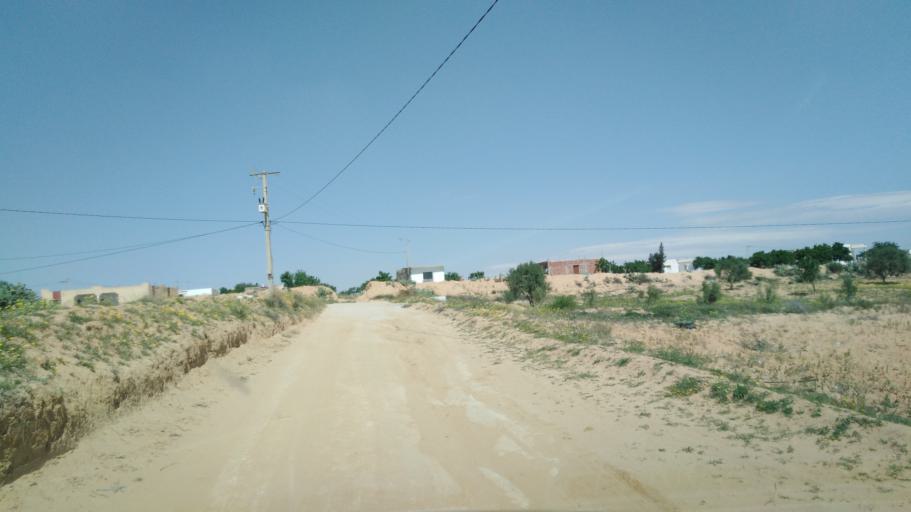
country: TN
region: Safaqis
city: Sfax
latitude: 34.7780
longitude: 10.5248
